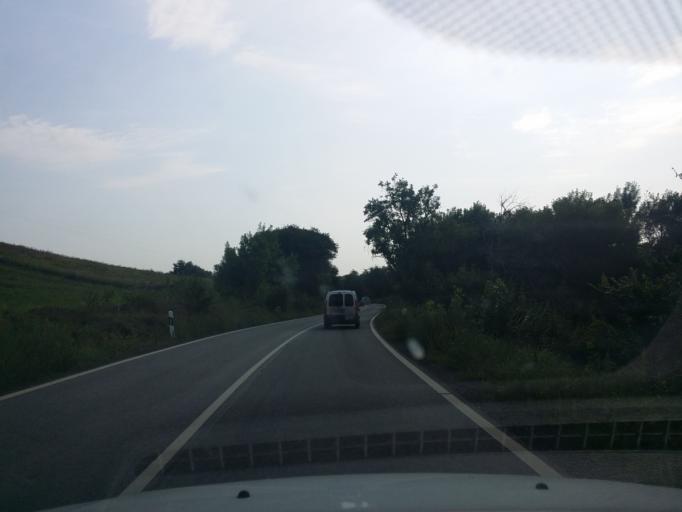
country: HU
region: Pest
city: Acsa
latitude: 47.7924
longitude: 19.3672
